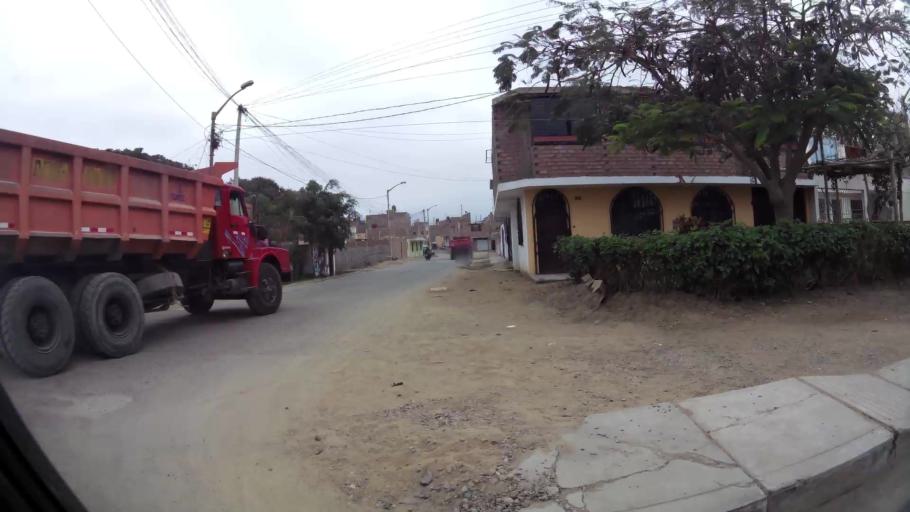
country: PE
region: La Libertad
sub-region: Provincia de Trujillo
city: La Esperanza
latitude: -8.0833
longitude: -79.0508
